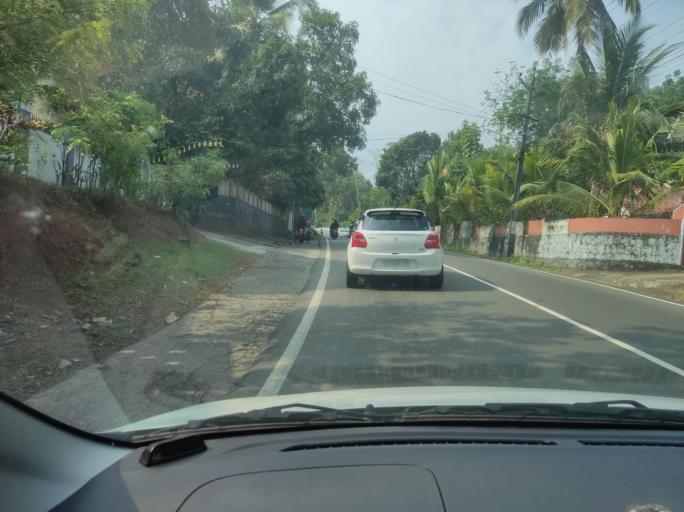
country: IN
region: Kerala
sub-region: Pattanamtitta
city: Adur
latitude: 9.1439
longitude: 76.7321
